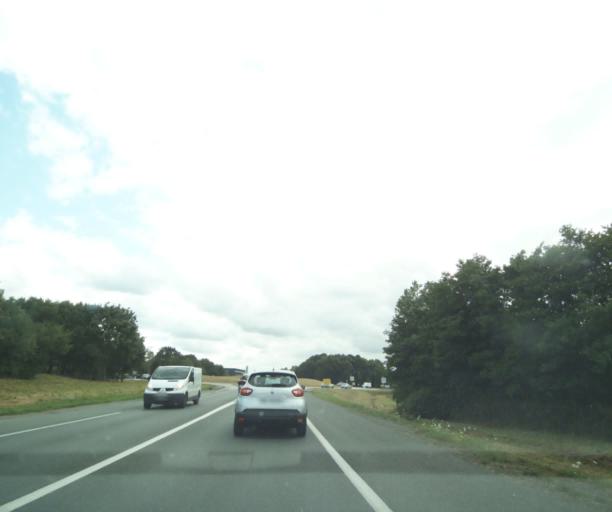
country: FR
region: Pays de la Loire
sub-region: Departement de la Vendee
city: Les Clouzeaux
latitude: 46.6500
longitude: -1.5107
